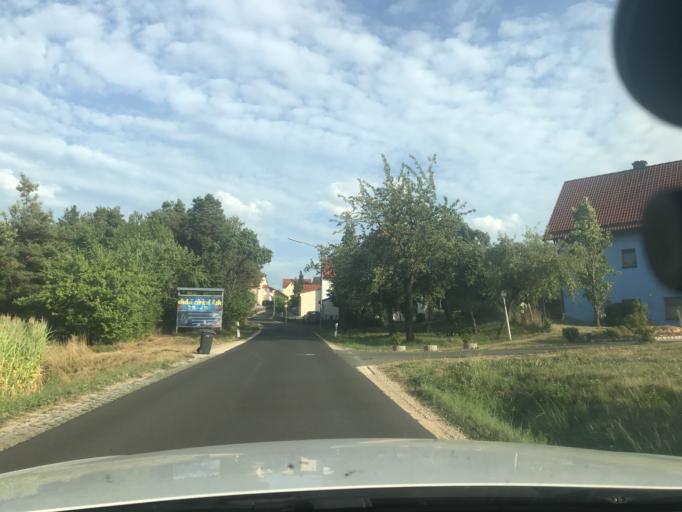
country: DE
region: Bavaria
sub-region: Upper Franconia
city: Pegnitz
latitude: 49.7707
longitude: 11.5980
